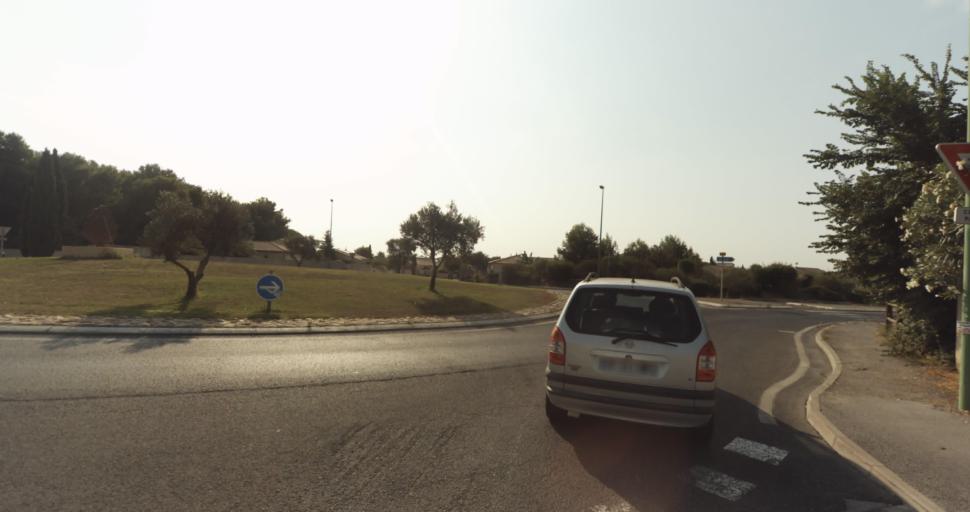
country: FR
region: Languedoc-Roussillon
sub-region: Departement des Pyrenees-Orientales
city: Latour-Bas-Elne
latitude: 42.6120
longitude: 3.0017
